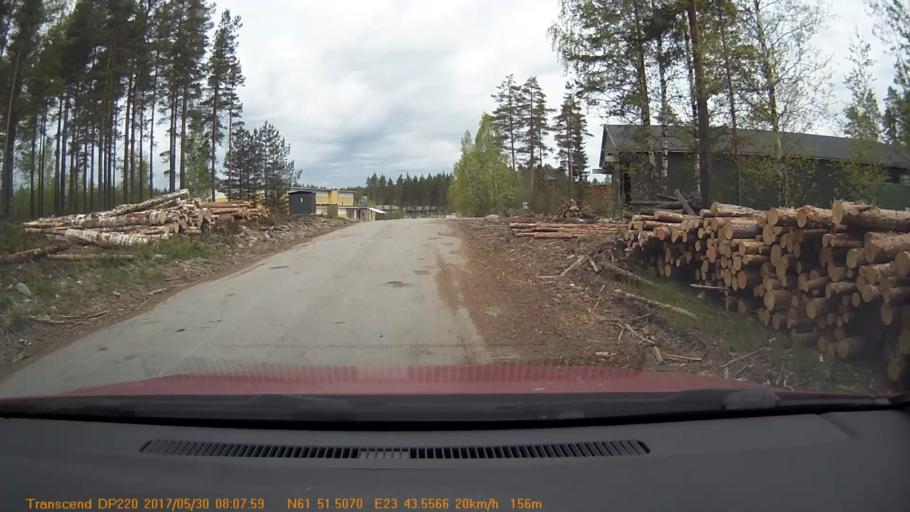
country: FI
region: Pirkanmaa
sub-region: Tampere
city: Kuru
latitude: 61.8584
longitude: 23.7261
